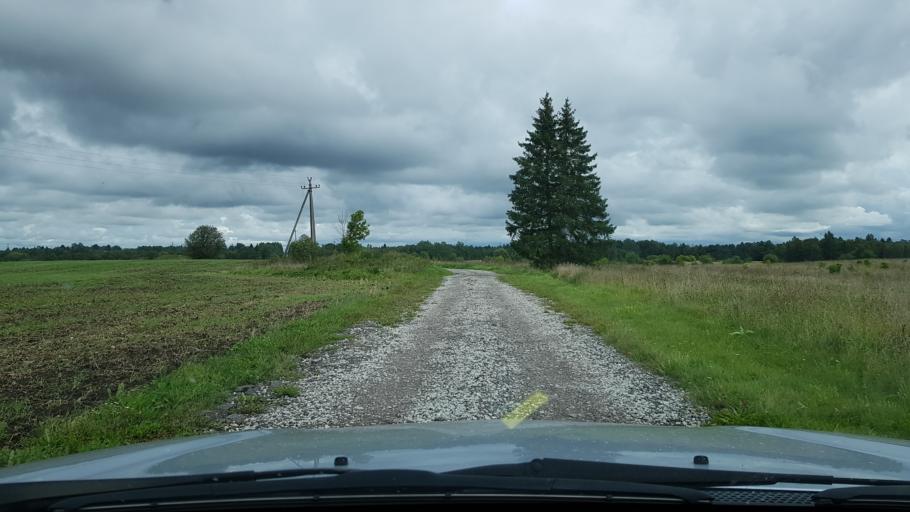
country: EE
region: Harju
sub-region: Rae vald
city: Vaida
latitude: 59.3506
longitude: 24.9801
